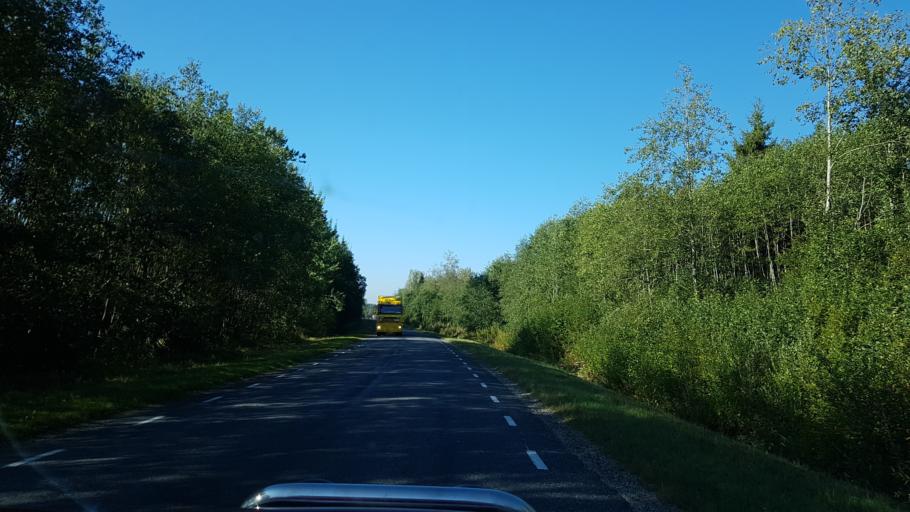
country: EE
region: Jogevamaa
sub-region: Jogeva linn
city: Jogeva
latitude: 58.6939
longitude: 26.3681
